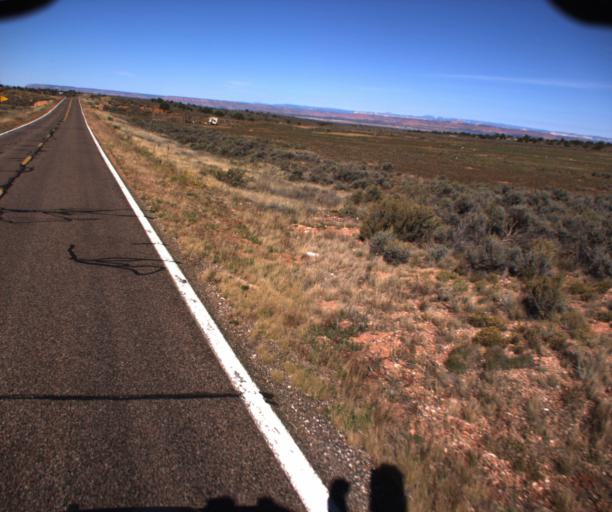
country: US
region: Arizona
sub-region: Coconino County
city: Fredonia
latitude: 36.8541
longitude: -112.2968
